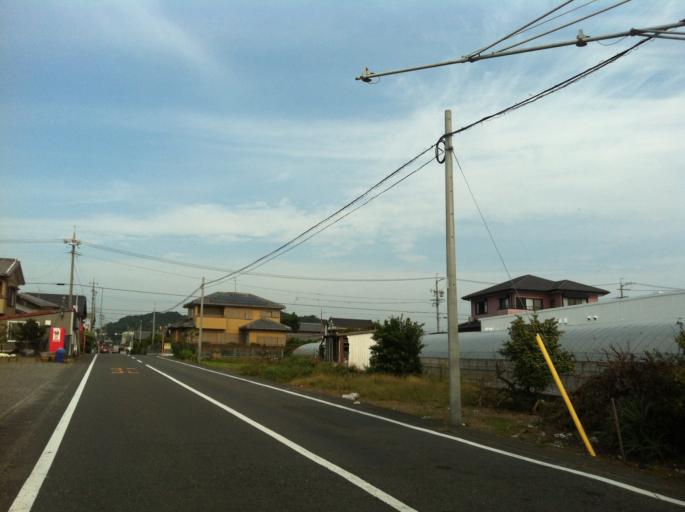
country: JP
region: Shizuoka
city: Sagara
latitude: 34.7382
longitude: 138.2312
